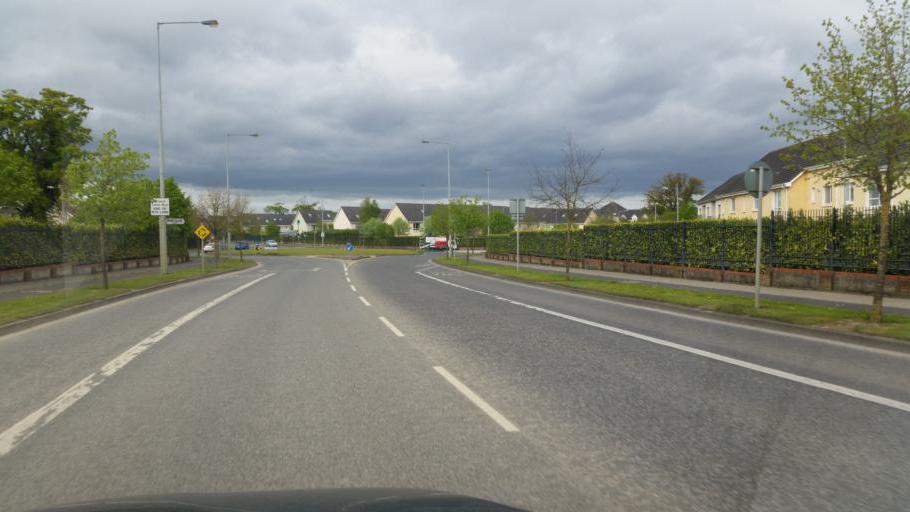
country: IE
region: Leinster
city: Hartstown
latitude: 53.3951
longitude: -6.4441
